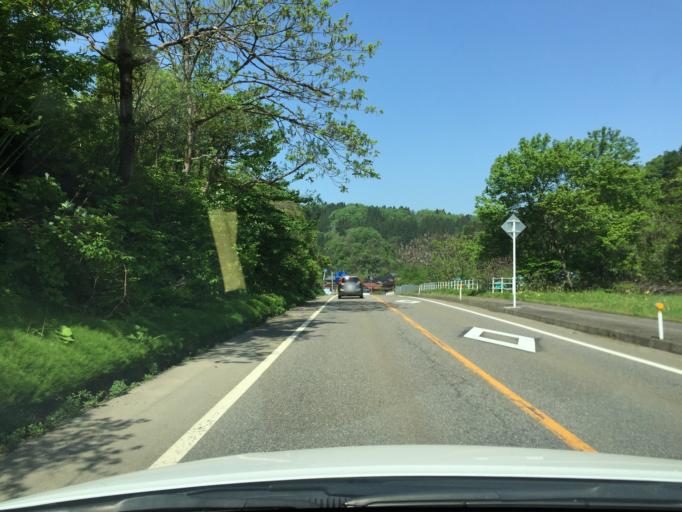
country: JP
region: Niigata
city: Kamo
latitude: 37.6334
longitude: 139.1011
